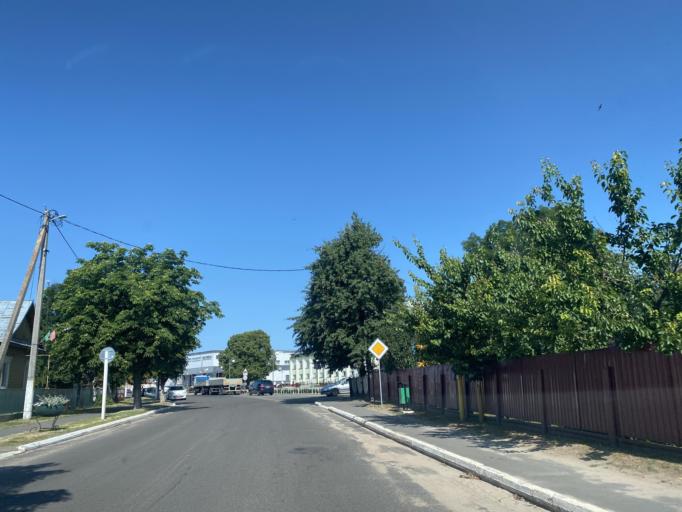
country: BY
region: Brest
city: Ivanava
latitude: 52.3161
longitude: 25.6109
